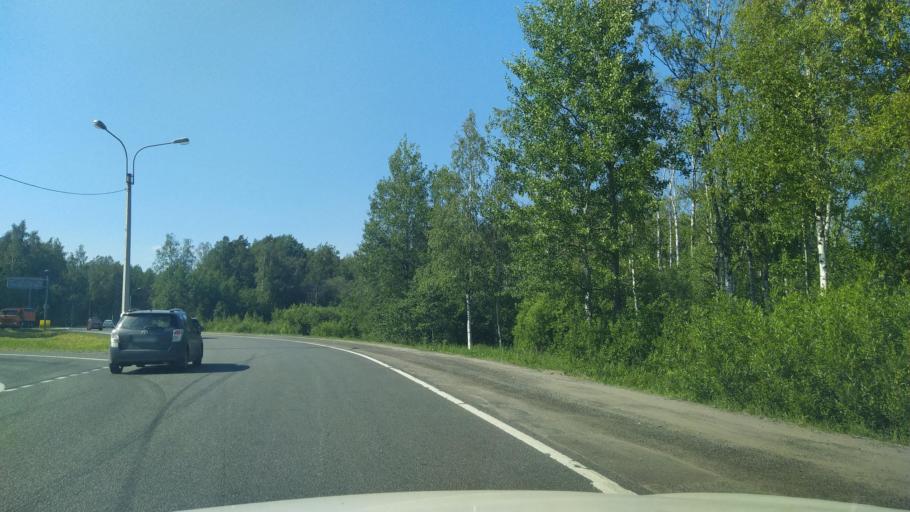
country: RU
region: St.-Petersburg
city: Beloostrov
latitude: 60.1406
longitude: 29.9882
